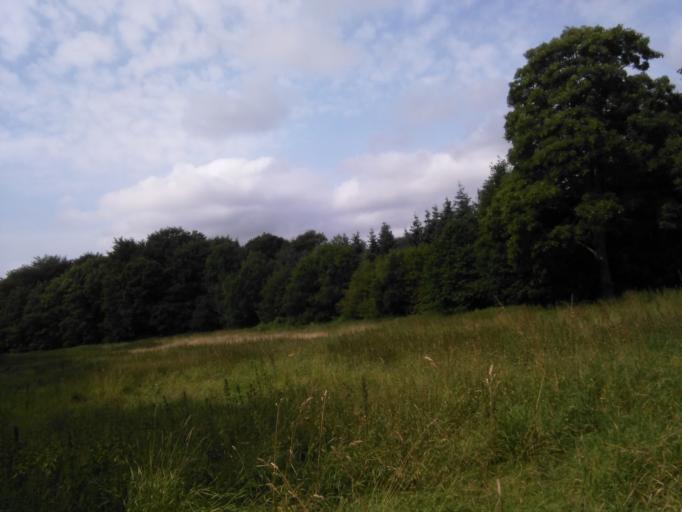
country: DK
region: Central Jutland
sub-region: Odder Kommune
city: Odder
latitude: 55.8830
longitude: 10.0489
